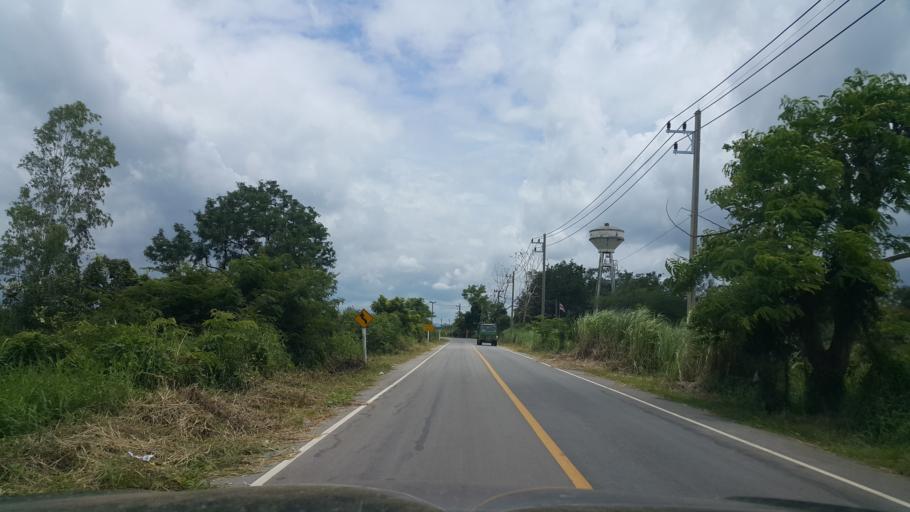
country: TH
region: Sukhothai
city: Kong Krailat
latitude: 16.9337
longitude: 99.9535
